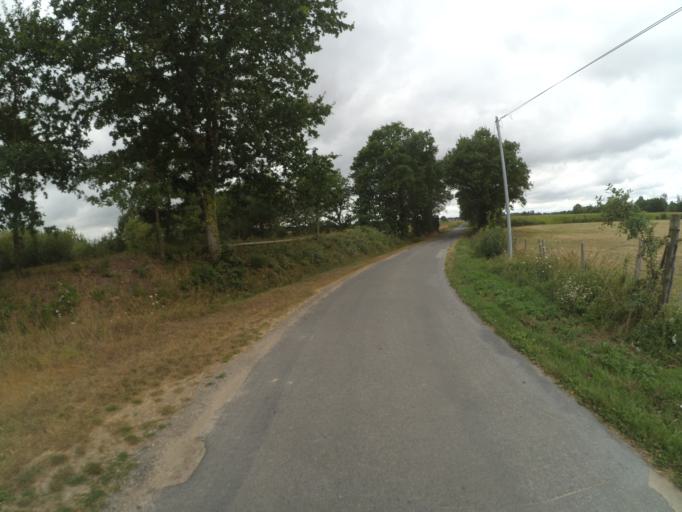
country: FR
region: Pays de la Loire
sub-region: Departement de la Loire-Atlantique
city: La Planche
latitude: 47.0009
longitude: -1.4488
